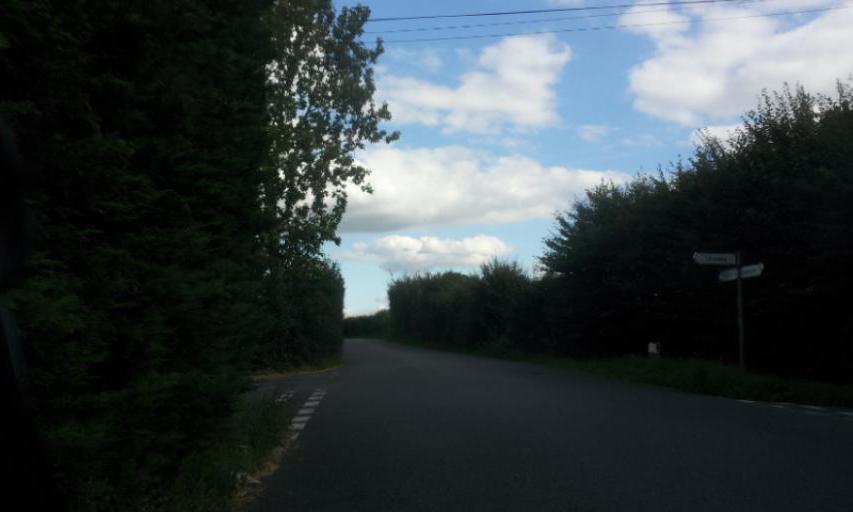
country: GB
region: England
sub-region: Kent
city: Headcorn
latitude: 51.1750
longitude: 0.5994
